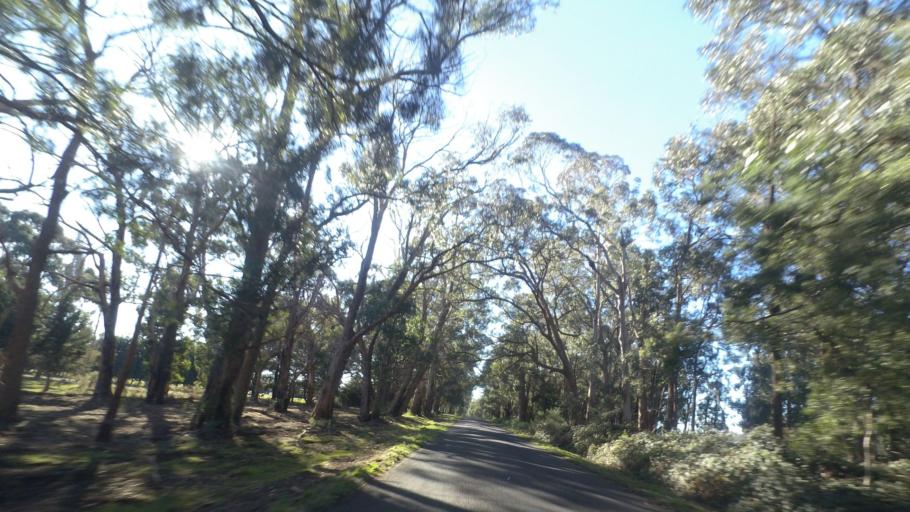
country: AU
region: Victoria
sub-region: Mount Alexander
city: Castlemaine
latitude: -37.3176
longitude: 144.3288
